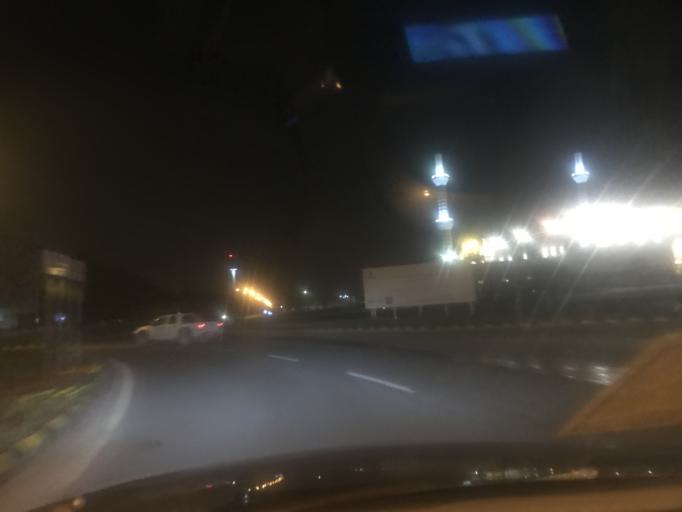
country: SA
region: Ar Riyad
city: Riyadh
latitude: 24.6929
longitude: 46.6039
